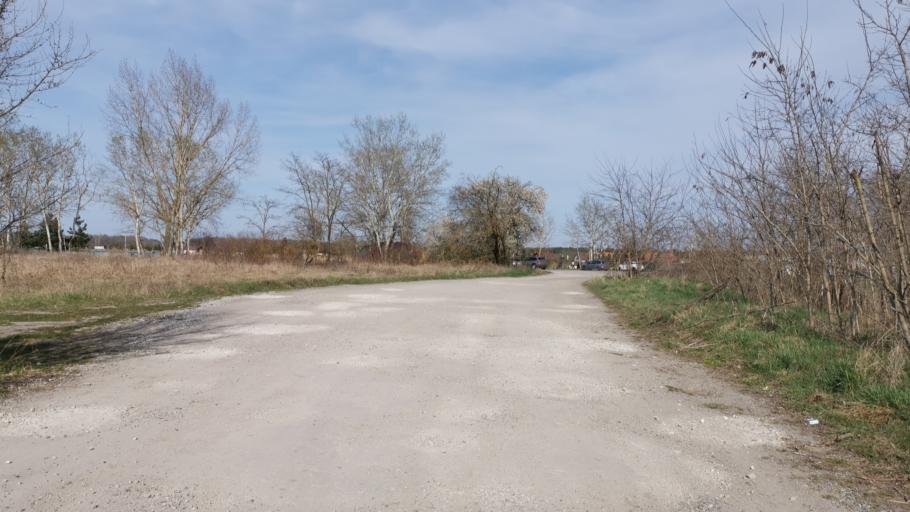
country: CZ
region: South Moravian
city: Tvrdonice
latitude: 48.7261
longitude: 17.0332
